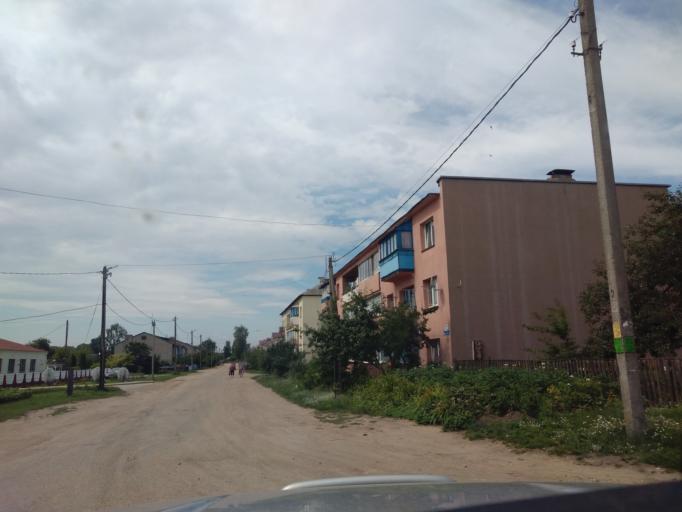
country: BY
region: Minsk
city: Kapyl'
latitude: 53.1405
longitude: 27.0923
